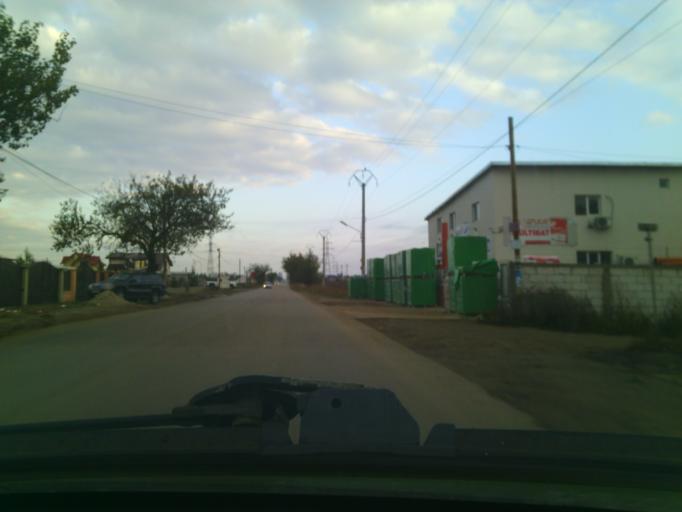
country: RO
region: Ilfov
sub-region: Comuna Berceni
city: Berceni
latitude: 44.3326
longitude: 26.1709
